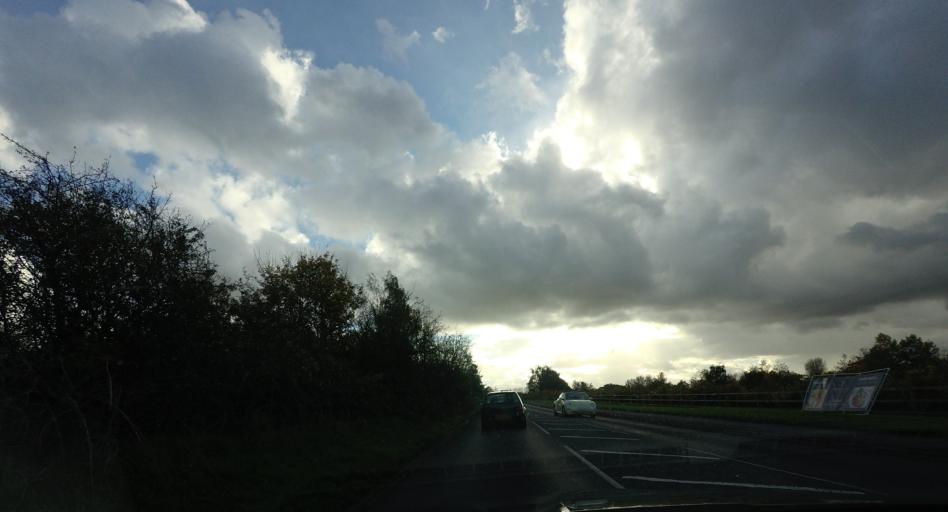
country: GB
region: England
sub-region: Kent
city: Swanley
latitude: 51.4125
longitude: 0.1647
